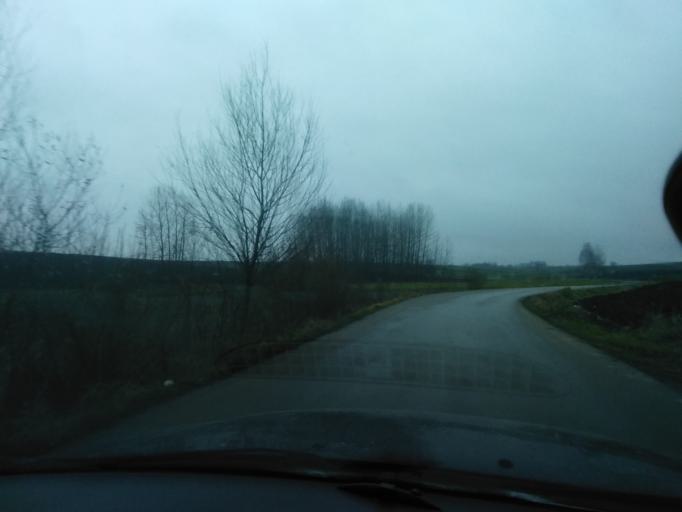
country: PL
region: Subcarpathian Voivodeship
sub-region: Powiat jaroslawski
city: Rokietnica
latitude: 49.9262
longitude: 22.6173
